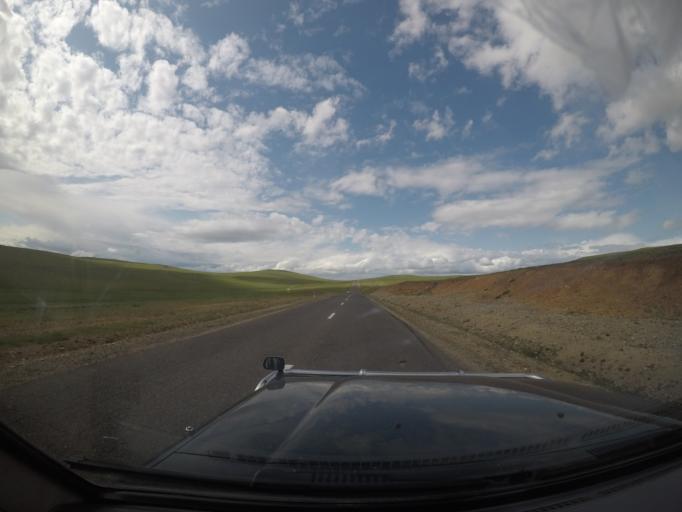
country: MN
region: Hentiy
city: Modot
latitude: 47.5701
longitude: 109.3076
